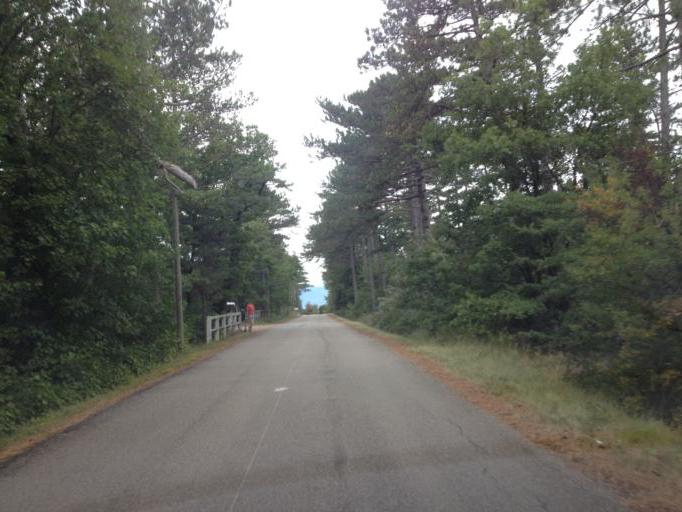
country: FR
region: Rhone-Alpes
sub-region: Departement de la Drome
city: Allan
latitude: 44.4729
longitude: 4.8096
